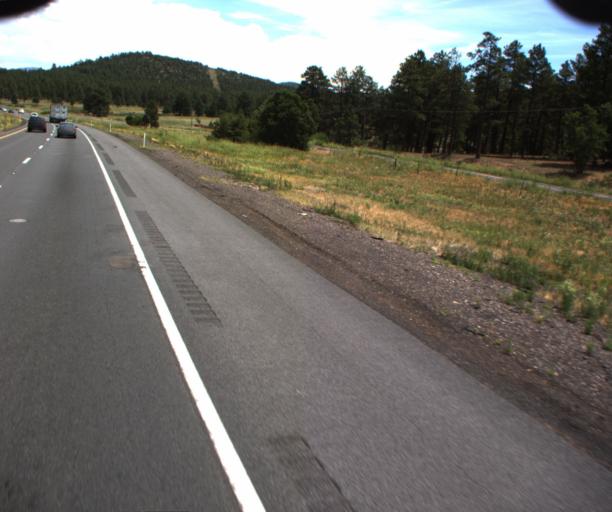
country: US
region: Arizona
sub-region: Coconino County
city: Williams
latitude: 35.2367
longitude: -112.2234
